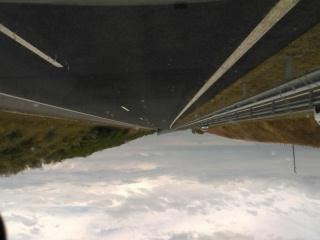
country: BG
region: Sliven
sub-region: Obshtina Sliven
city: Kermen
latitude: 42.5097
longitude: 26.3545
